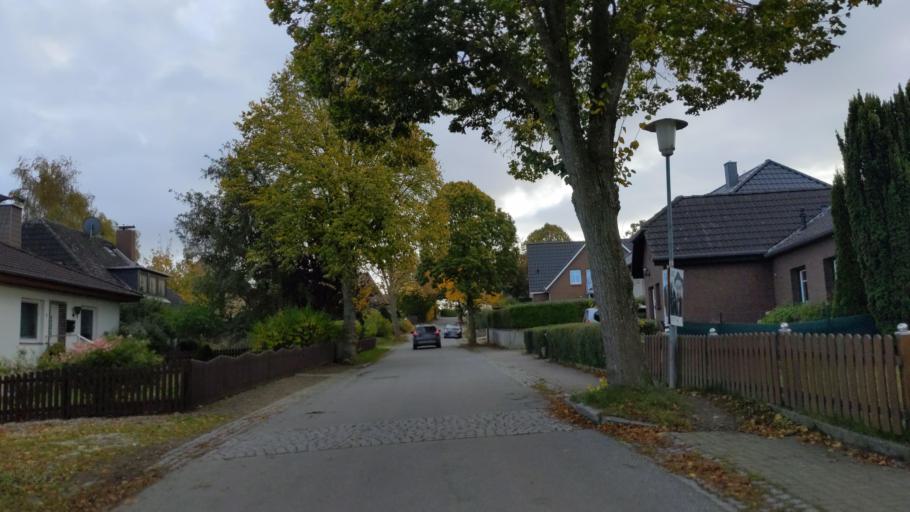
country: DE
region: Schleswig-Holstein
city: Kasseedorf
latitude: 54.1344
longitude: 10.7021
